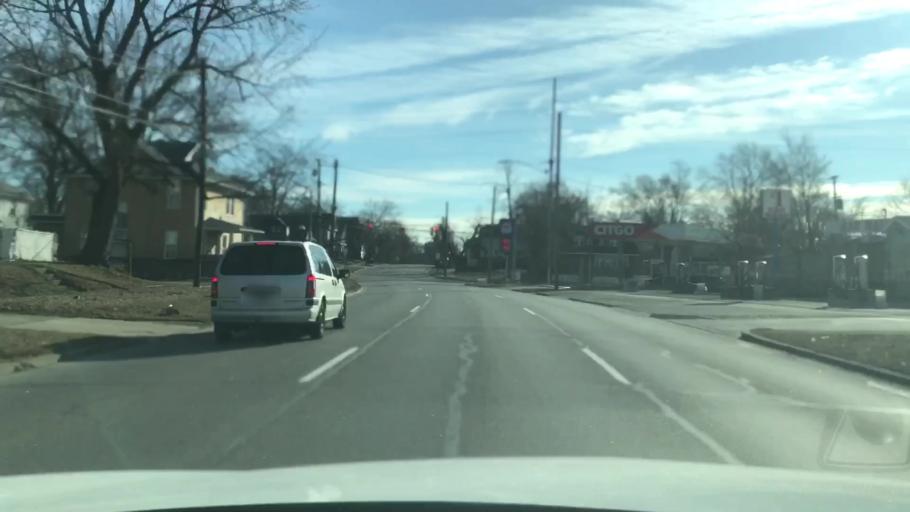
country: US
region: Michigan
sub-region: Oakland County
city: Pontiac
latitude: 42.6452
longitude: -83.3049
